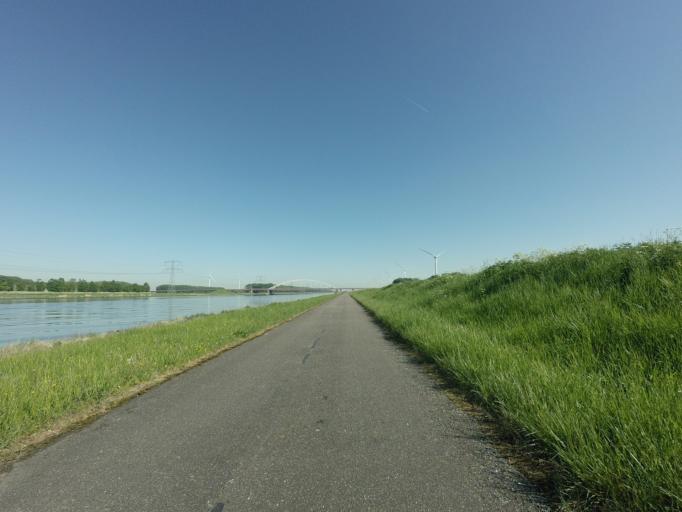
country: NL
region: North Brabant
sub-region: Gemeente Woensdrecht
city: Woensdrecht
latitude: 51.3972
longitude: 4.2422
